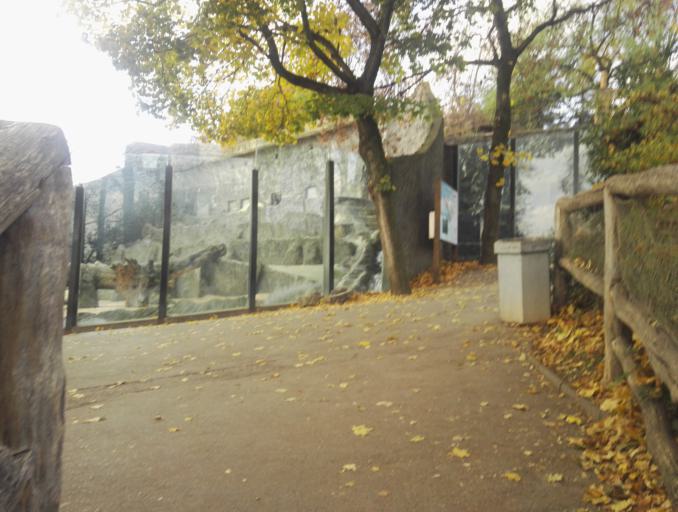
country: CZ
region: Praha
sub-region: Praha 1
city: Mala Strana
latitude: 50.1176
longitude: 14.4097
